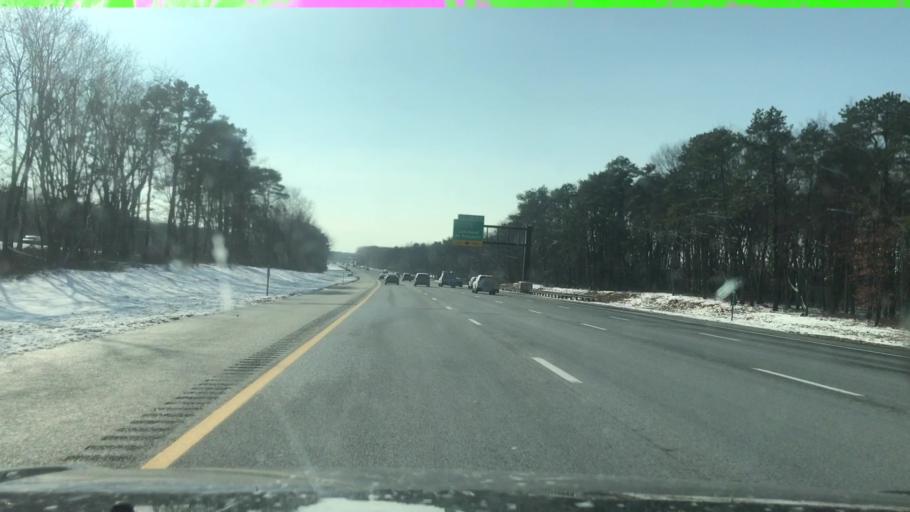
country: US
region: New Jersey
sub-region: Monmouth County
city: Ramtown
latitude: 40.1128
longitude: -74.1331
